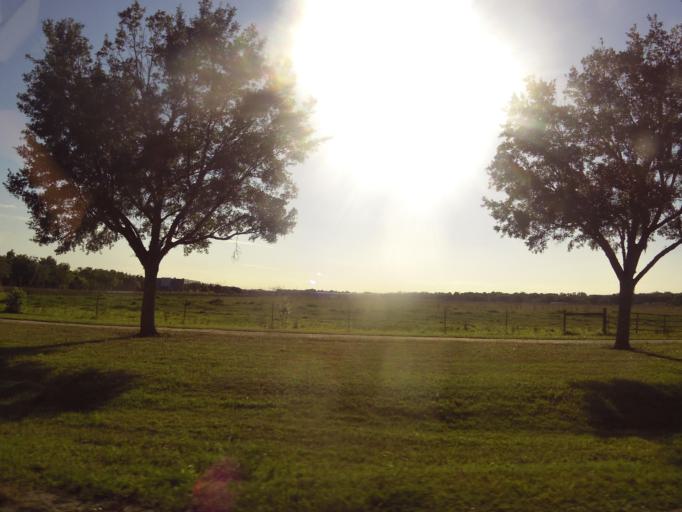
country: US
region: Florida
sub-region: Duval County
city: Jacksonville
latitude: 30.4518
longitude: -81.5582
